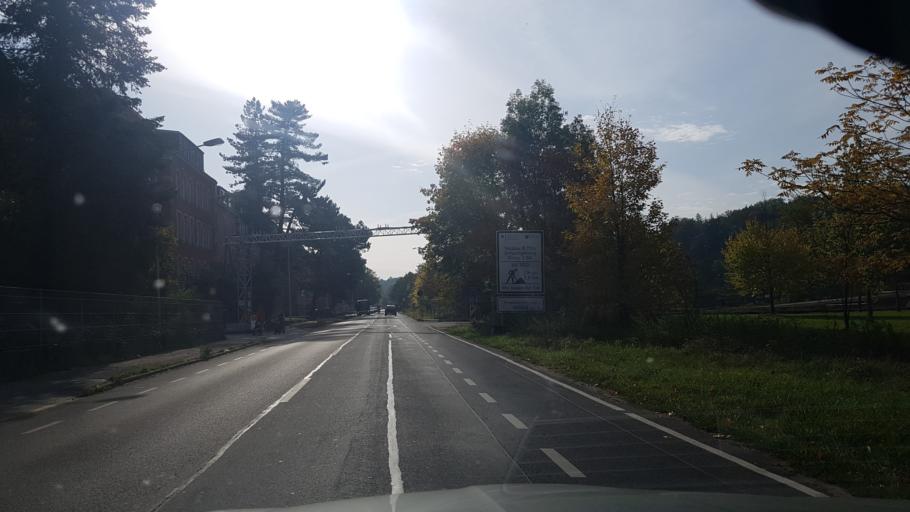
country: DE
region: Saxony
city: Pirna
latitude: 50.9424
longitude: 13.9438
